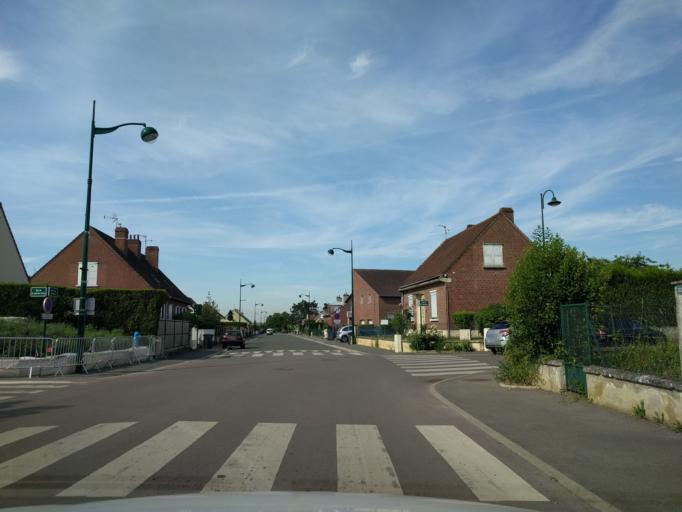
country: FR
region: Picardie
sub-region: Departement de l'Oise
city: Tille
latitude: 49.4624
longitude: 2.1109
